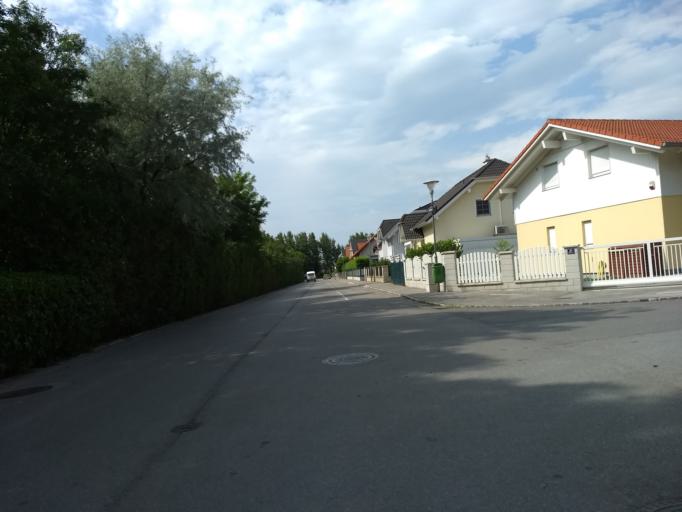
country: AT
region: Lower Austria
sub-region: Politischer Bezirk Modling
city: Neu-Guntramsdorf
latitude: 48.0592
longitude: 16.3194
